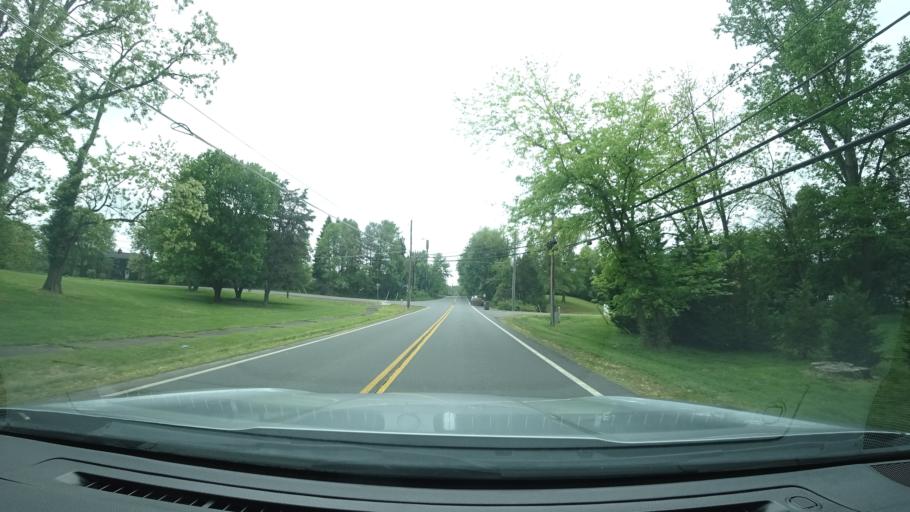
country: US
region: Virginia
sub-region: Fairfax County
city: Oak Hill
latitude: 38.9027
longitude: -77.3567
